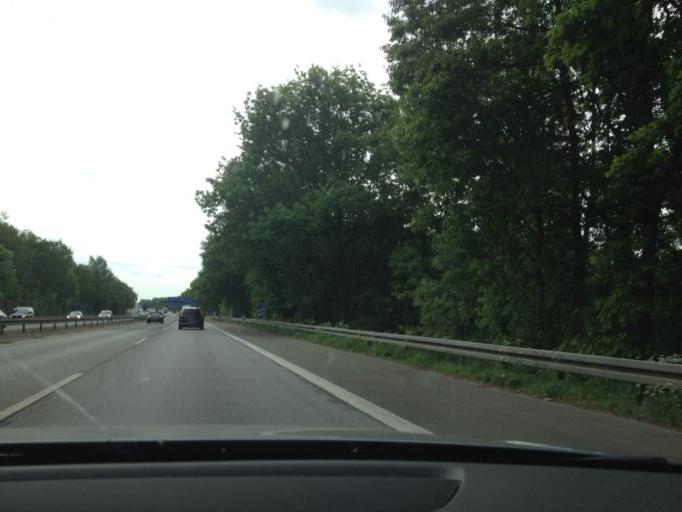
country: DE
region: North Rhine-Westphalia
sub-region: Regierungsbezirk Dusseldorf
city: Dinslaken
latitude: 51.5436
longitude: 6.8251
